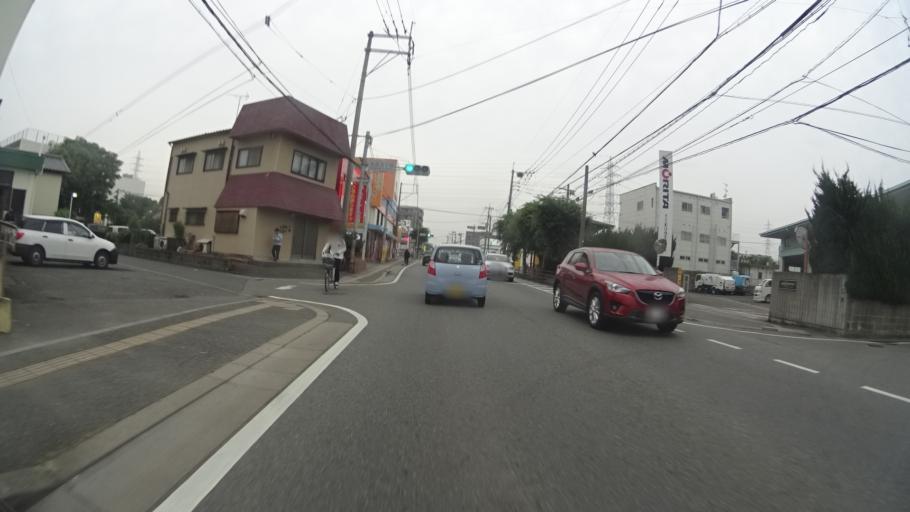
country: JP
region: Fukuoka
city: Onojo
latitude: 33.5338
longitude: 130.4827
